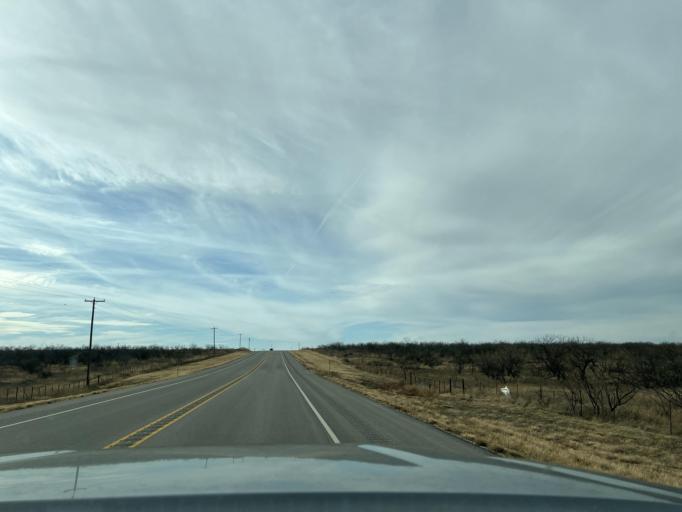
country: US
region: Texas
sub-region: Jones County
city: Anson
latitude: 32.7506
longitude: -99.6958
